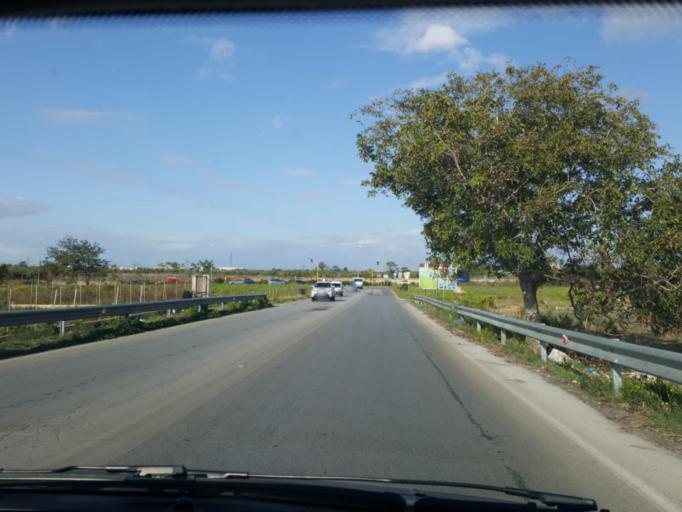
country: IT
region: Apulia
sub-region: Provincia di Bari
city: Capurso
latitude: 41.0567
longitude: 16.9165
